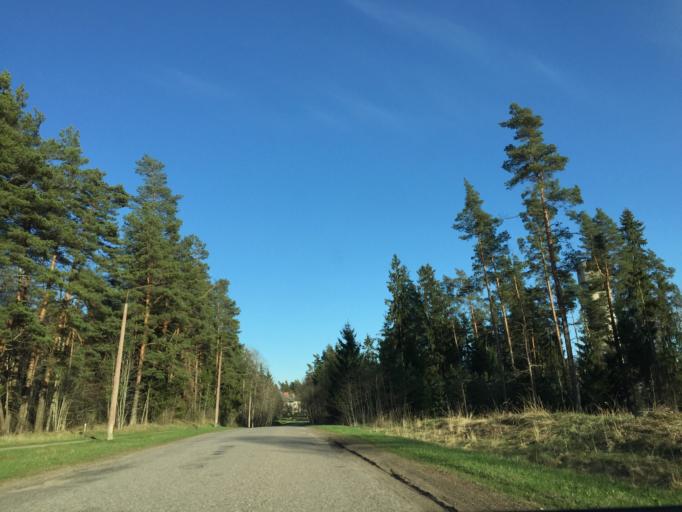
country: LV
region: Valkas Rajons
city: Valka
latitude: 57.7887
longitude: 25.9904
